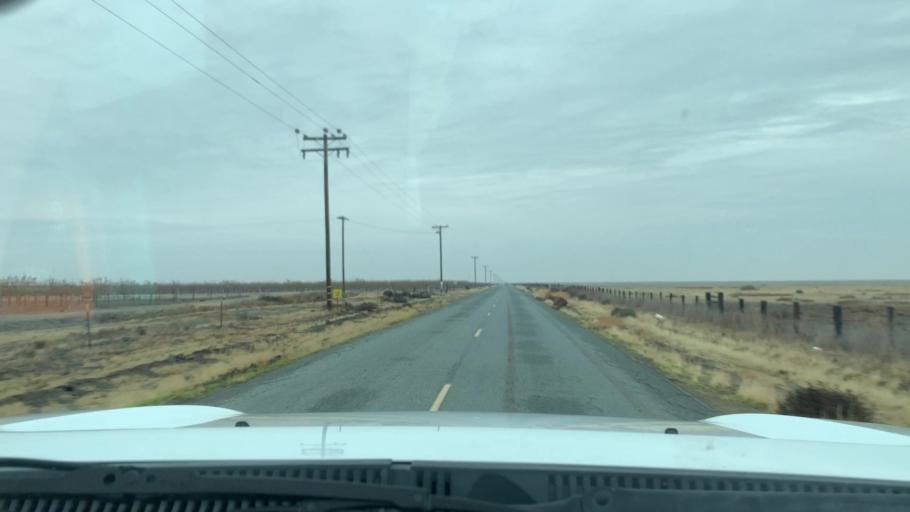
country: US
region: California
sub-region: Tulare County
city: Alpaugh
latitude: 35.7608
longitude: -119.5629
